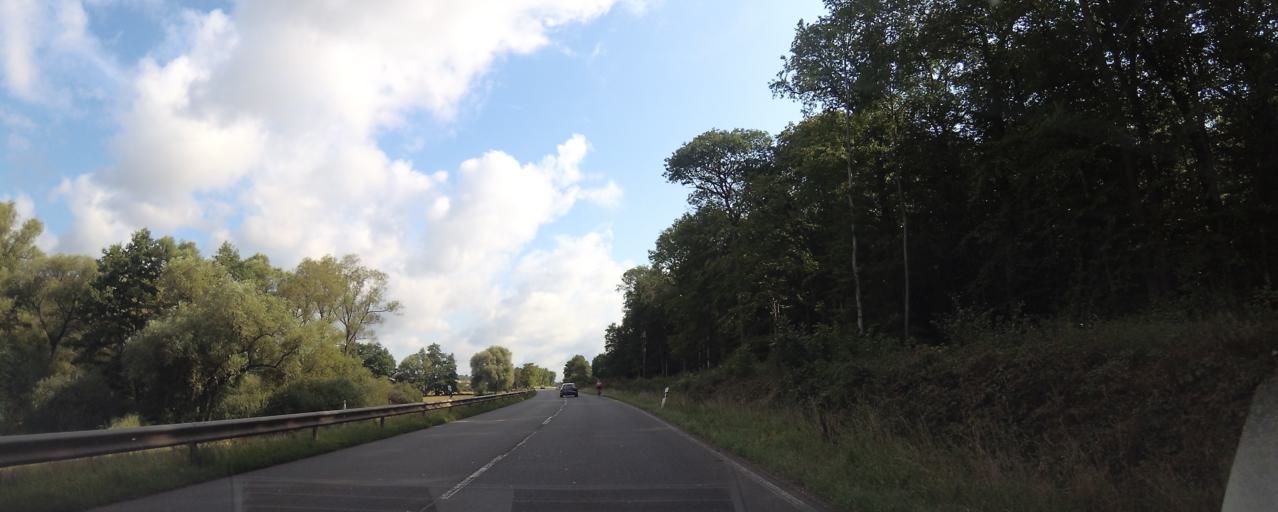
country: DE
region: Rheinland-Pfalz
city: Fohren
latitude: 49.8398
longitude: 6.7704
